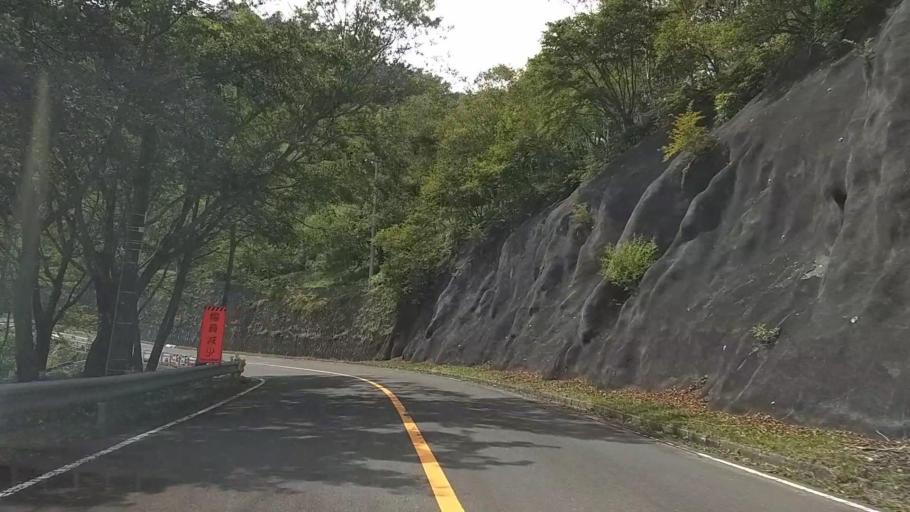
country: JP
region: Tochigi
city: Nikko
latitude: 36.7161
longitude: 139.4837
